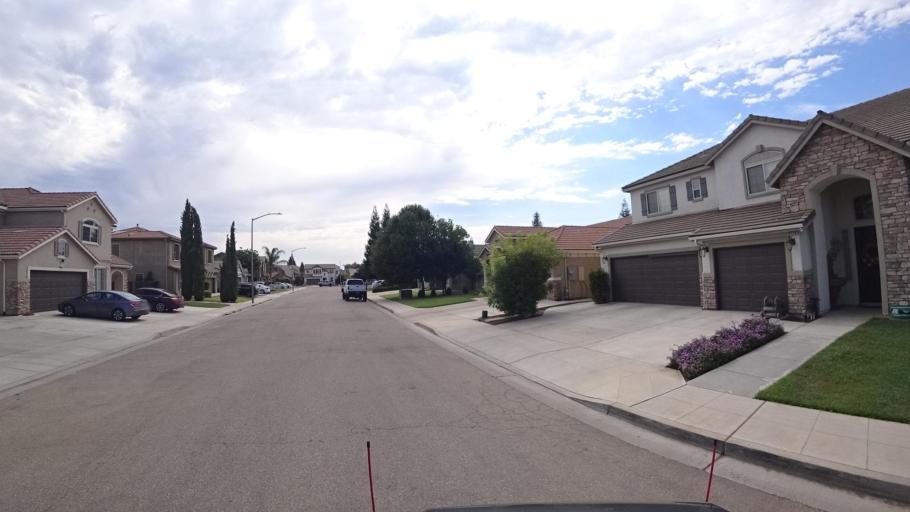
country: US
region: California
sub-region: Fresno County
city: Tarpey Village
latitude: 36.7782
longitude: -119.6678
